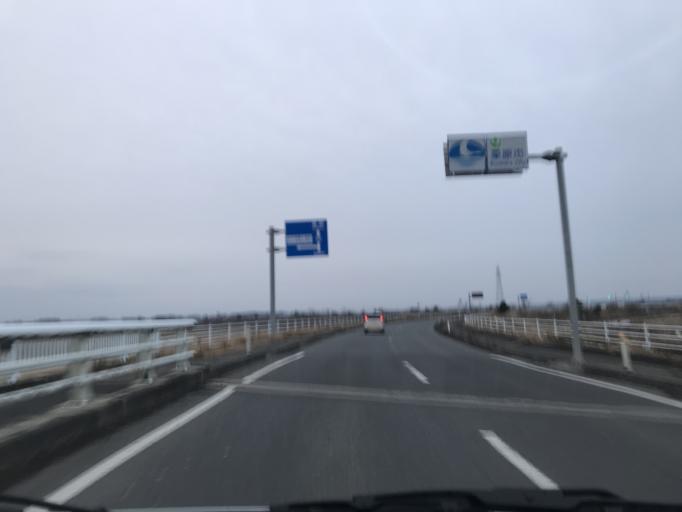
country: JP
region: Miyagi
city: Wakuya
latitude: 38.7243
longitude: 141.1491
